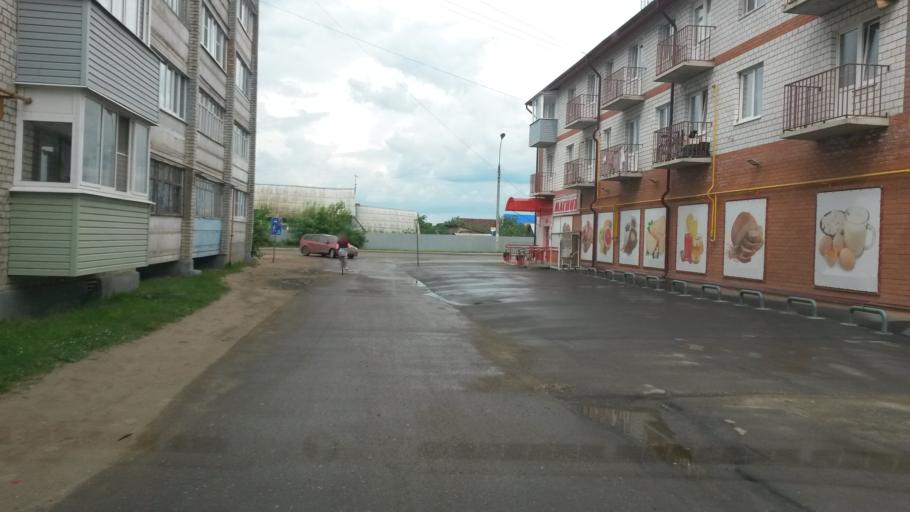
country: RU
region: Jaroslavl
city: Gavrilov-Yam
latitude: 57.3058
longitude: 39.8645
